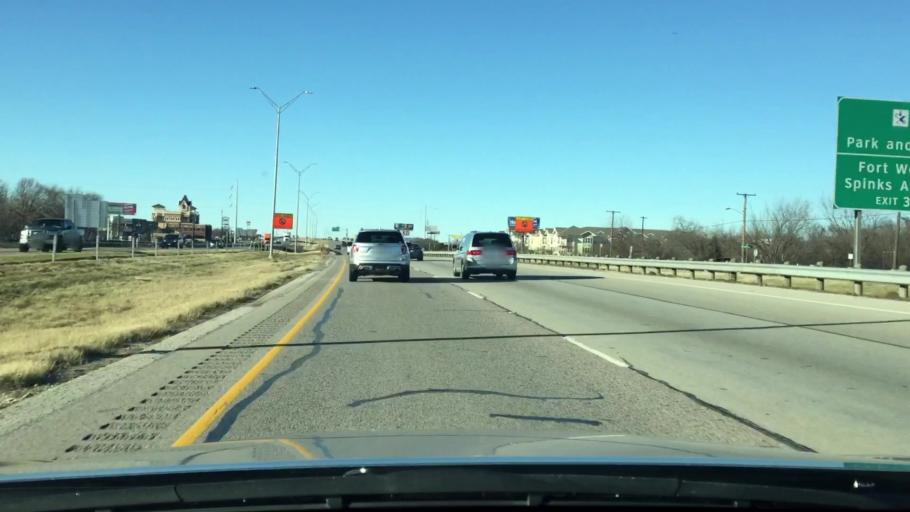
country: US
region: Texas
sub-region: Johnson County
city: Burleson
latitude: 32.5388
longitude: -97.3125
